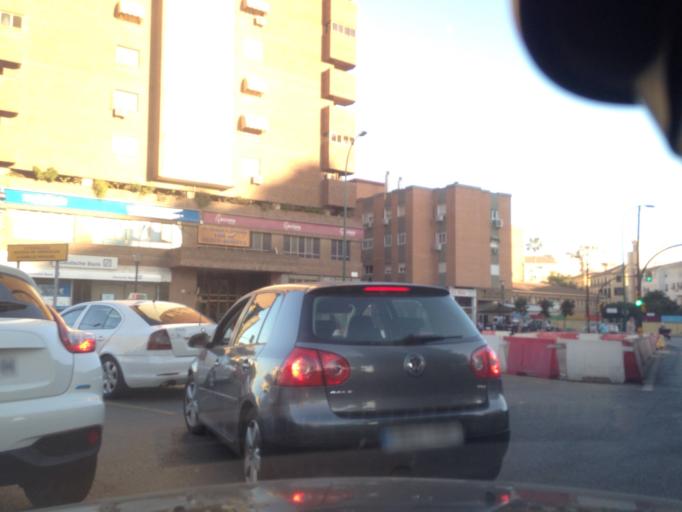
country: ES
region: Andalusia
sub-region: Provincia de Malaga
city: Malaga
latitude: 36.7166
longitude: -4.4297
